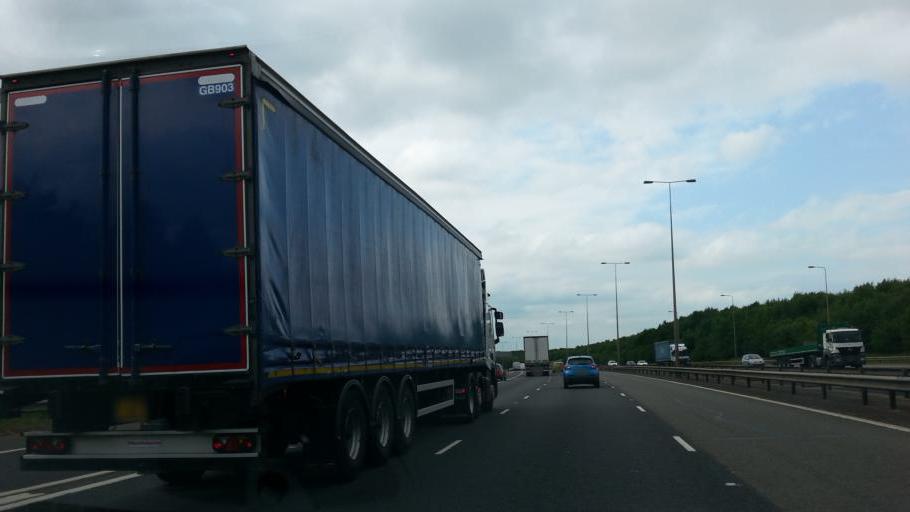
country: GB
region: England
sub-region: Cambridgeshire
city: Stilton
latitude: 52.5077
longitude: -0.2944
